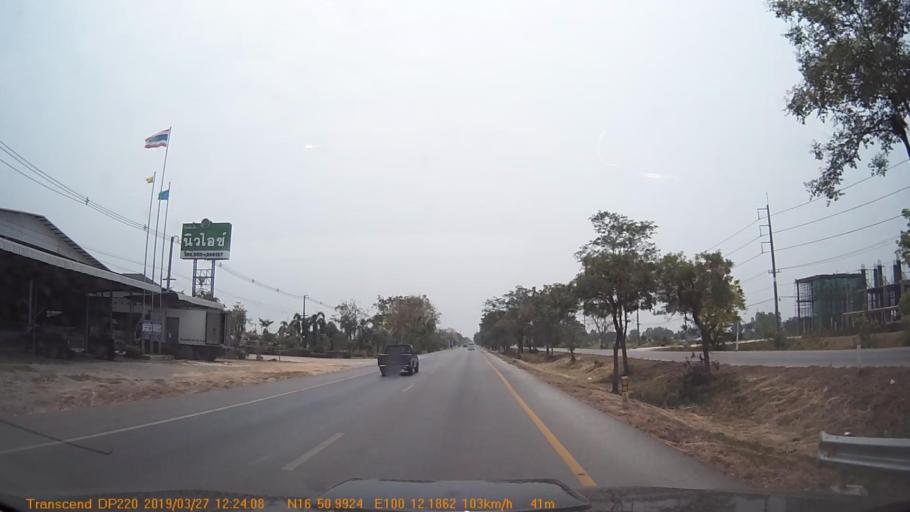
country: TH
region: Phitsanulok
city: Phitsanulok
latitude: 16.8496
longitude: 100.2031
